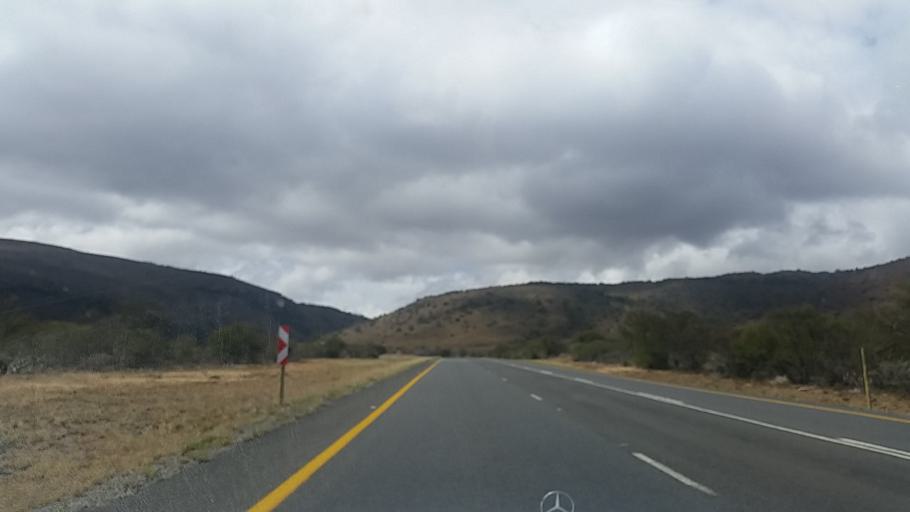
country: ZA
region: Eastern Cape
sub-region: Cacadu District Municipality
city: Graaff-Reinet
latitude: -31.9767
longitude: 24.7069
